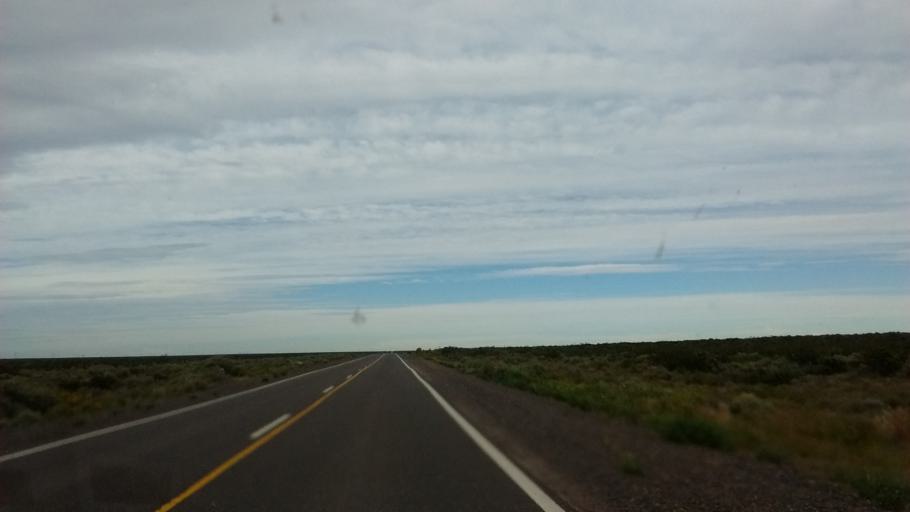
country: AR
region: Rio Negro
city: Contraalmirante Cordero
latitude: -38.4716
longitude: -68.0505
